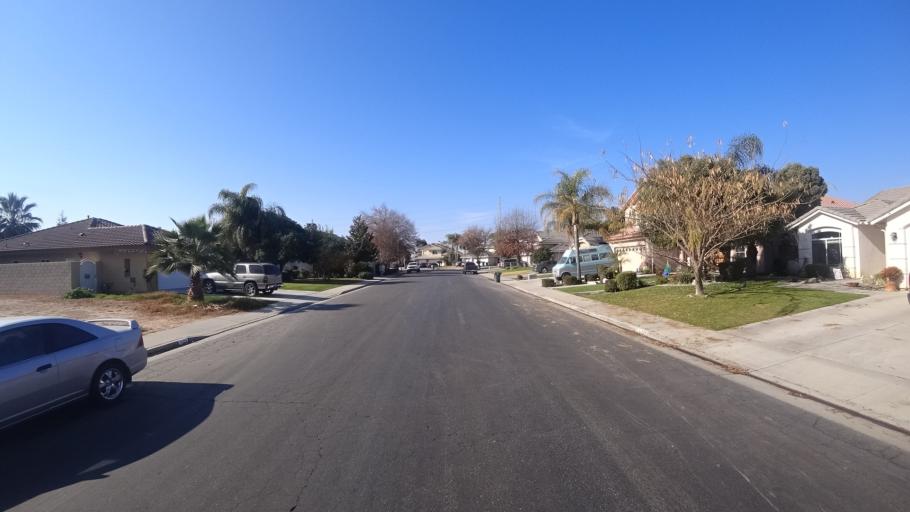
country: US
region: California
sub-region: Kern County
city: Greenacres
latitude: 35.3172
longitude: -119.1263
